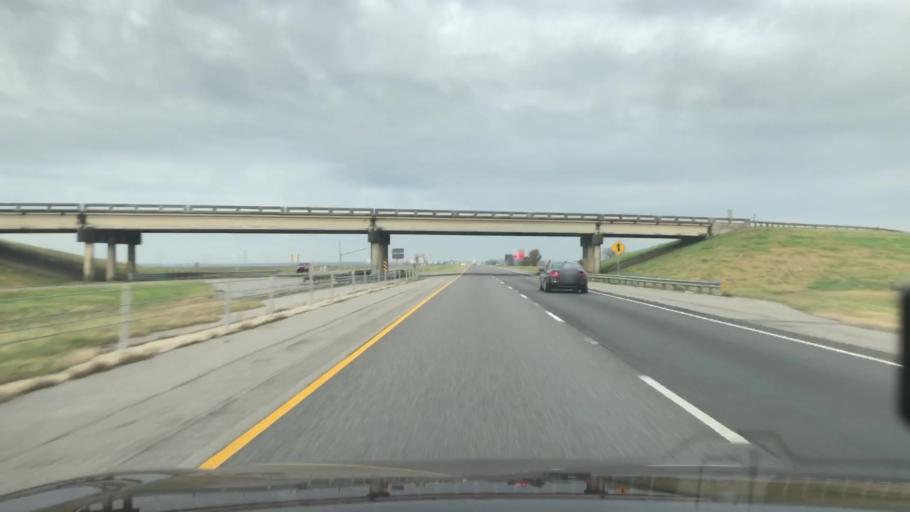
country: US
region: Mississippi
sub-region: Warren County
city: Vicksburg
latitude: 32.3226
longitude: -90.9582
